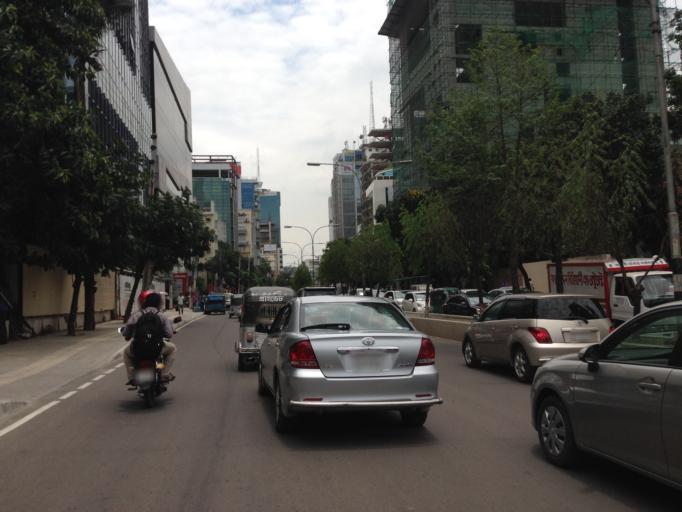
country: BD
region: Dhaka
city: Paltan
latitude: 23.7848
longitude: 90.4171
